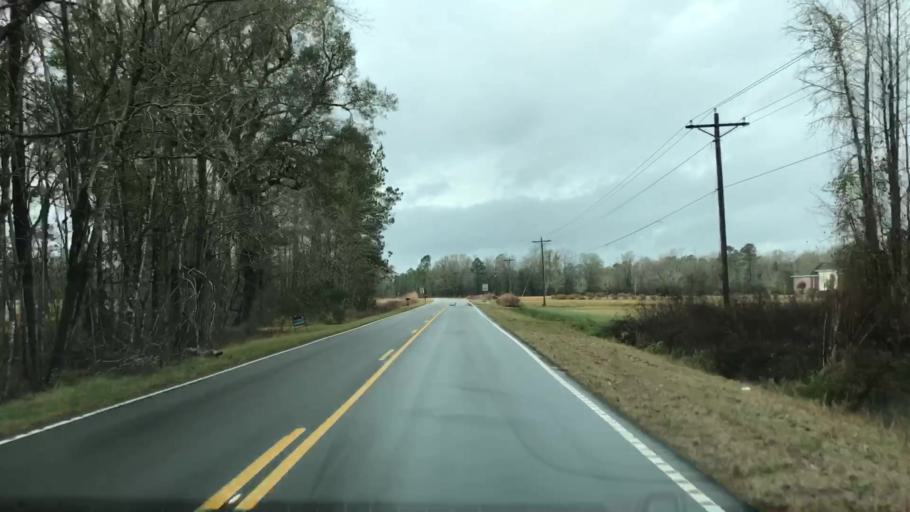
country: US
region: South Carolina
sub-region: Florence County
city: Johnsonville
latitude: 33.6746
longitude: -79.3305
